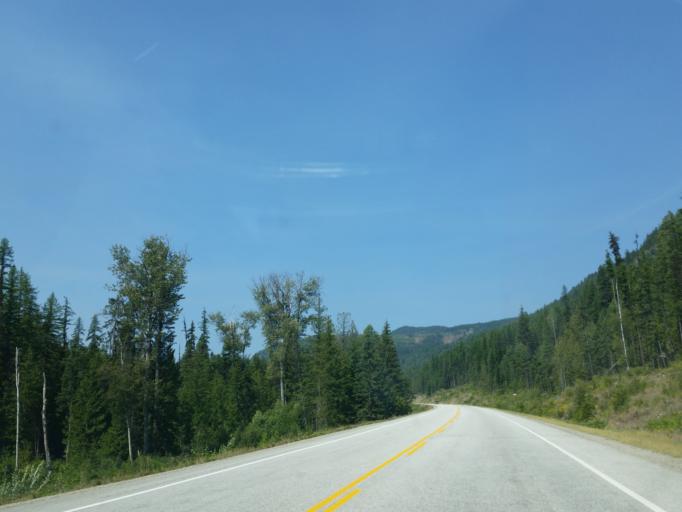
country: CA
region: British Columbia
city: Castlegar
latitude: 49.2963
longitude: -117.7669
